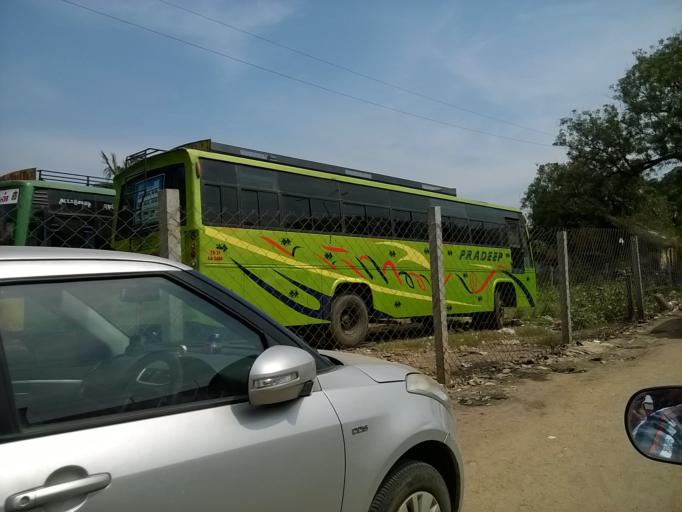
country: IN
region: Tamil Nadu
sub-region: Cuddalore
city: Panruti
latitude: 11.7715
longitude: 79.5540
